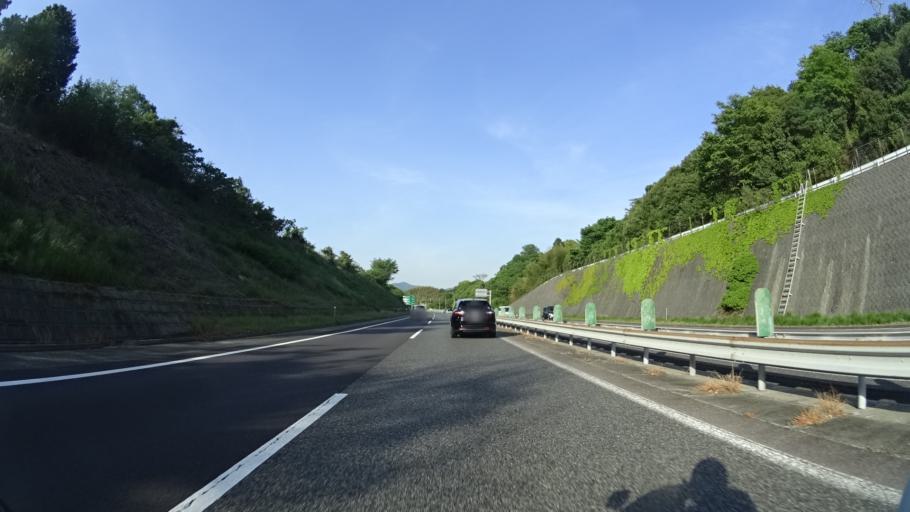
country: JP
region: Ehime
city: Kawanoecho
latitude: 33.9808
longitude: 133.5816
